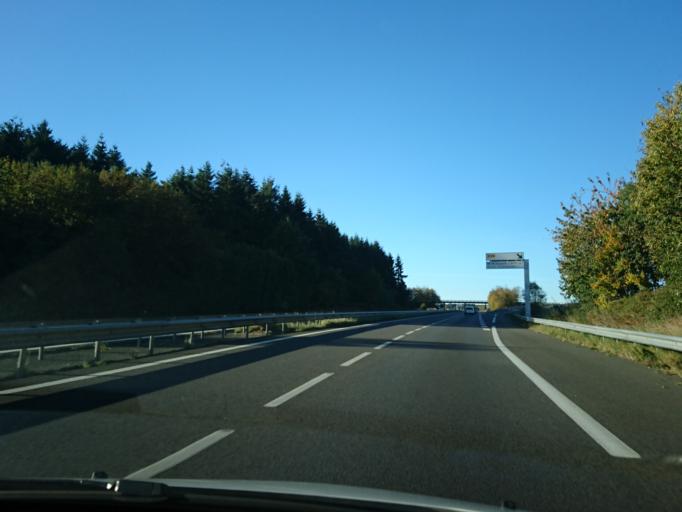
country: FR
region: Brittany
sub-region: Departement d'Ille-et-Vilaine
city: Montauban-de-Bretagne
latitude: 48.1934
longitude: -2.0237
